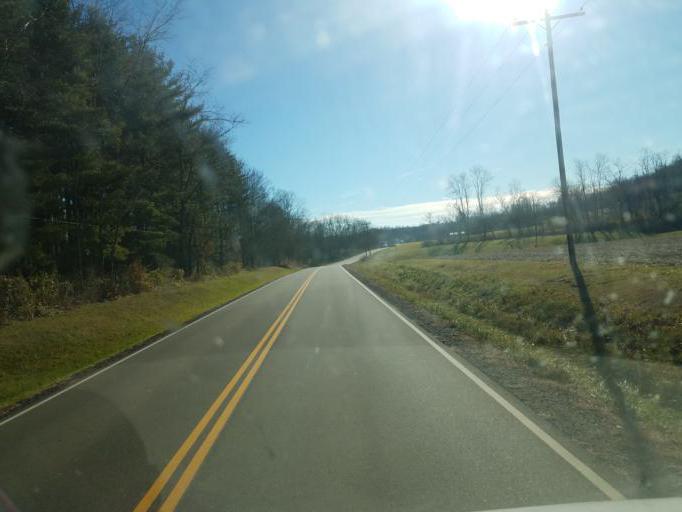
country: US
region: Ohio
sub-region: Muskingum County
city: Dresden
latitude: 40.1884
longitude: -82.0372
